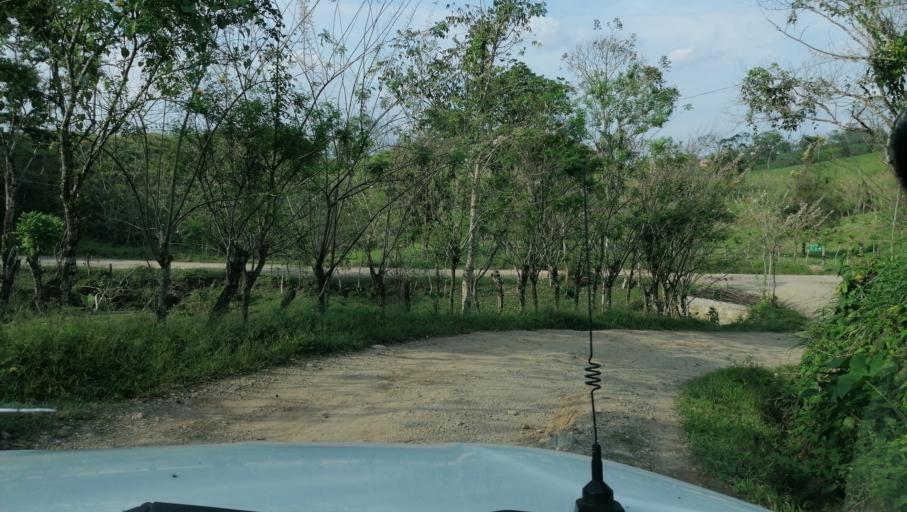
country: MX
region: Chiapas
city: Ostuacan
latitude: 17.4842
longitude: -93.2409
